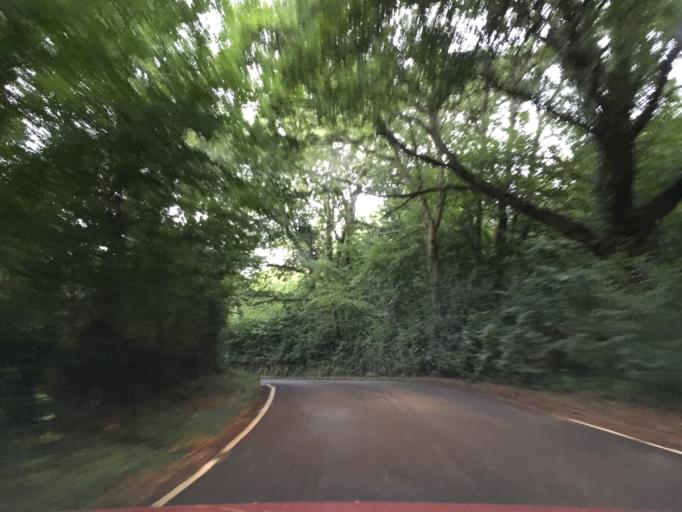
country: GB
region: Wales
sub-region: Monmouthshire
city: Llangwm
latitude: 51.6579
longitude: -2.8557
